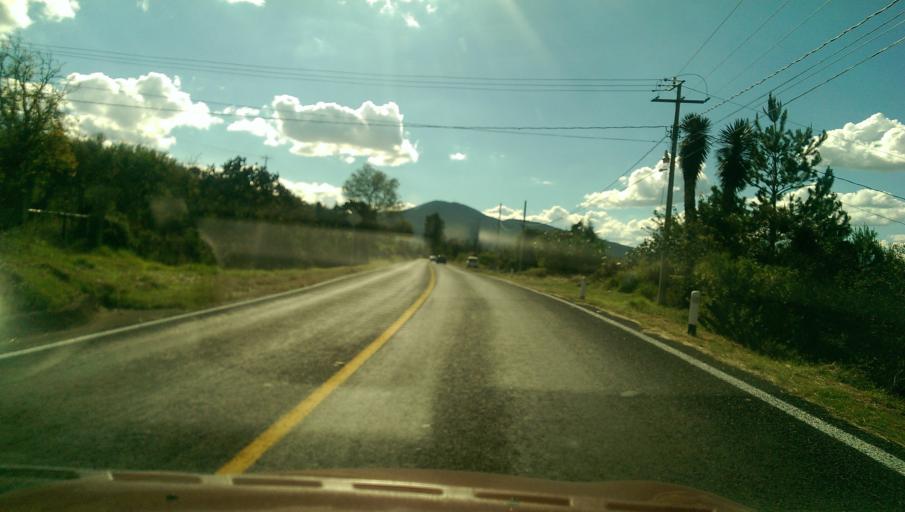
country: MX
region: Michoacan
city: Santa Fe de la Laguna
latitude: 19.6400
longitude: -101.5466
